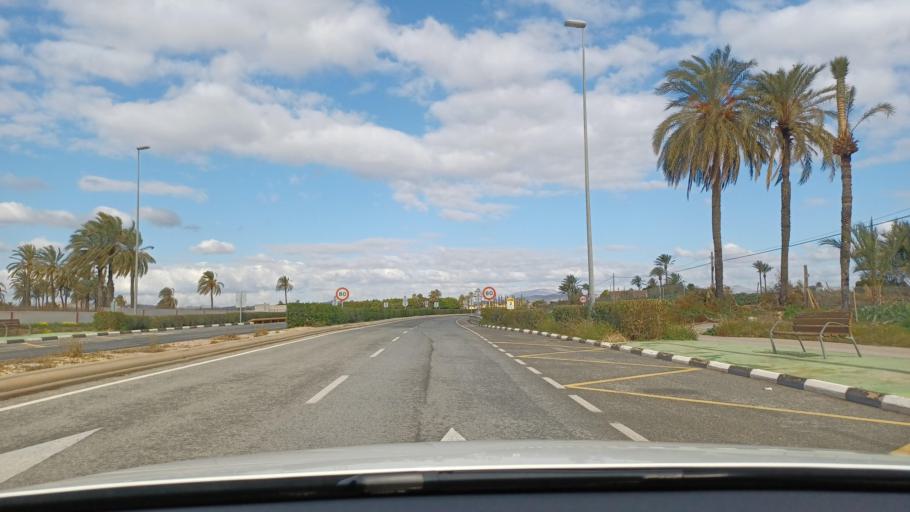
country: ES
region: Valencia
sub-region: Provincia de Alicante
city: Elche
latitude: 38.2320
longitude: -0.7000
